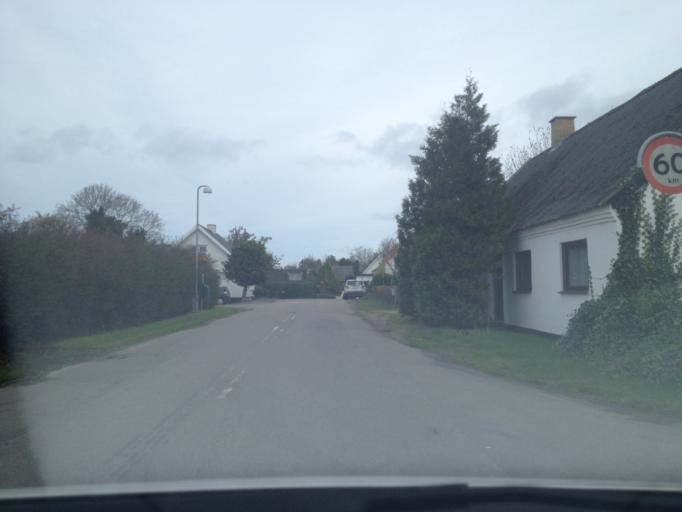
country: DK
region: Zealand
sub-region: Odsherred Kommune
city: Hojby
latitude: 55.9320
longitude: 11.6045
